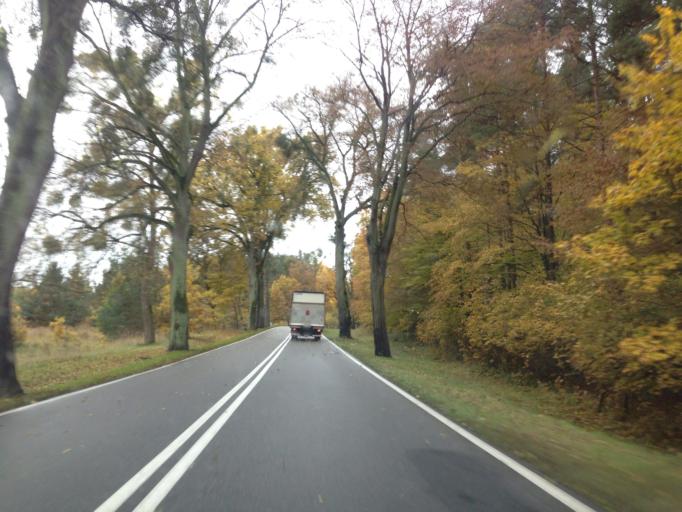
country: PL
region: Pomeranian Voivodeship
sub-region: Powiat kwidzynski
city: Ryjewo
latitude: 53.8590
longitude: 19.0013
